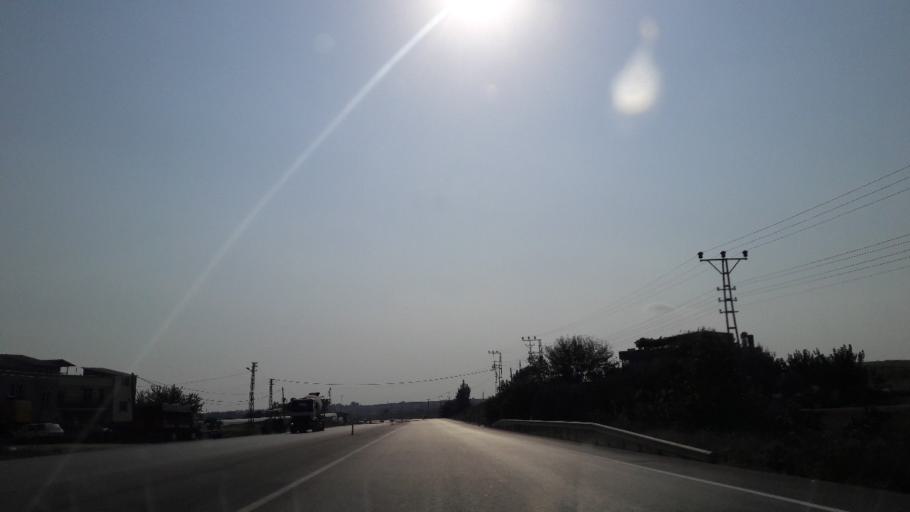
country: TR
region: Adana
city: Yuregir
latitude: 37.0675
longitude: 35.4516
